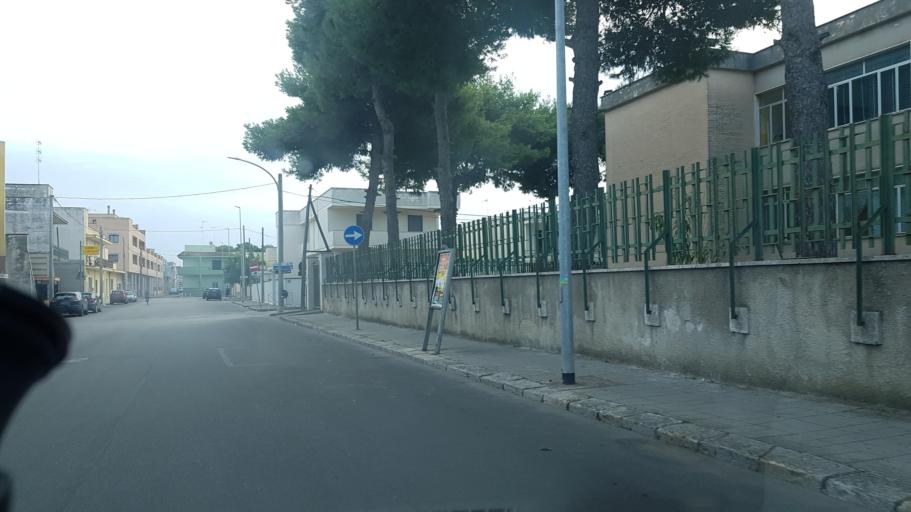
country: IT
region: Apulia
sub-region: Provincia di Lecce
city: Trepuzzi
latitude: 40.4106
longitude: 18.0704
